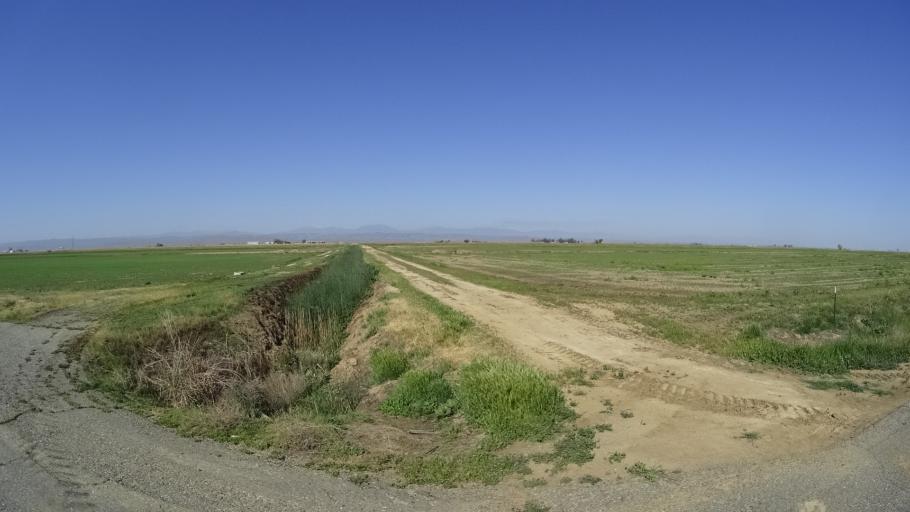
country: US
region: California
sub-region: Glenn County
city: Willows
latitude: 39.4179
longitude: -122.1941
